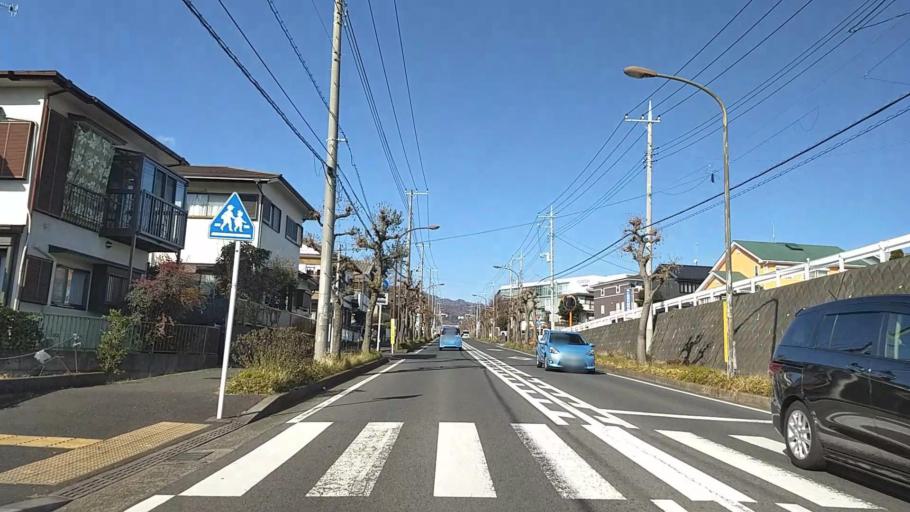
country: JP
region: Kanagawa
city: Isehara
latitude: 35.4008
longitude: 139.2977
